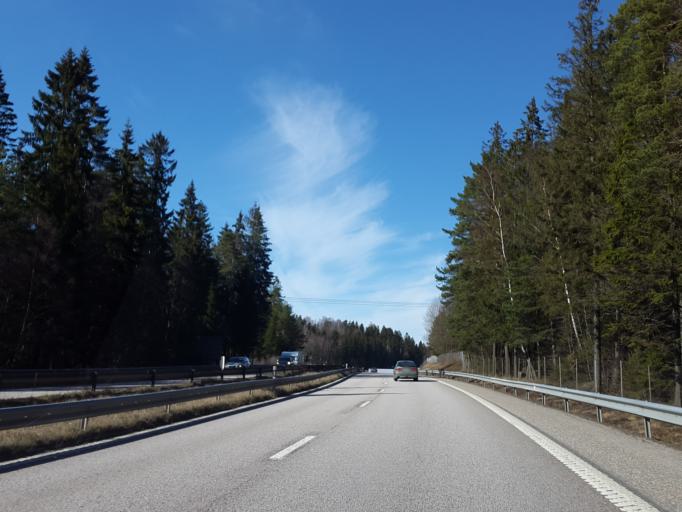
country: SE
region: Vaestra Goetaland
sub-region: Alingsas Kommun
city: Ingared
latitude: 57.8813
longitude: 12.4923
